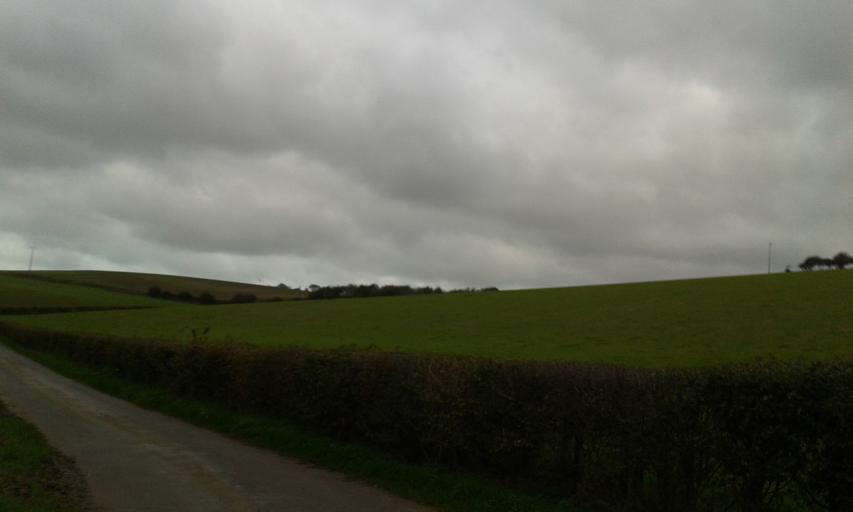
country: FR
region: Nord-Pas-de-Calais
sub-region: Departement du Pas-de-Calais
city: Ferques
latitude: 50.8731
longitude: 1.7360
